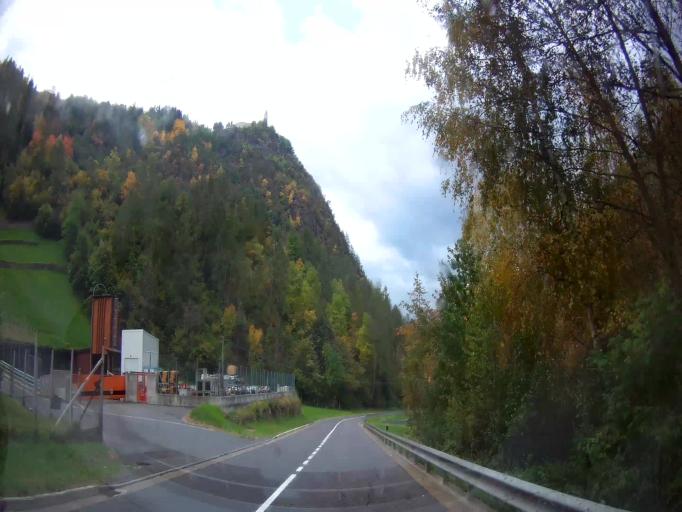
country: IT
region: Trentino-Alto Adige
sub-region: Bolzano
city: Certosa
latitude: 46.6909
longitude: 10.9284
